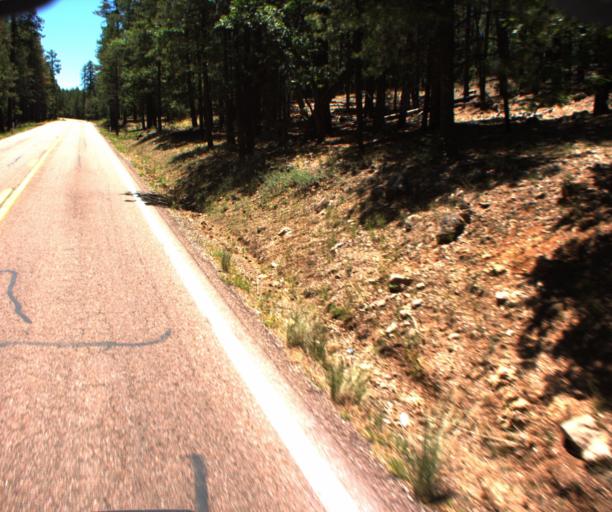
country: US
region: Arizona
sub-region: Gila County
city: Pine
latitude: 34.5198
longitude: -111.3423
